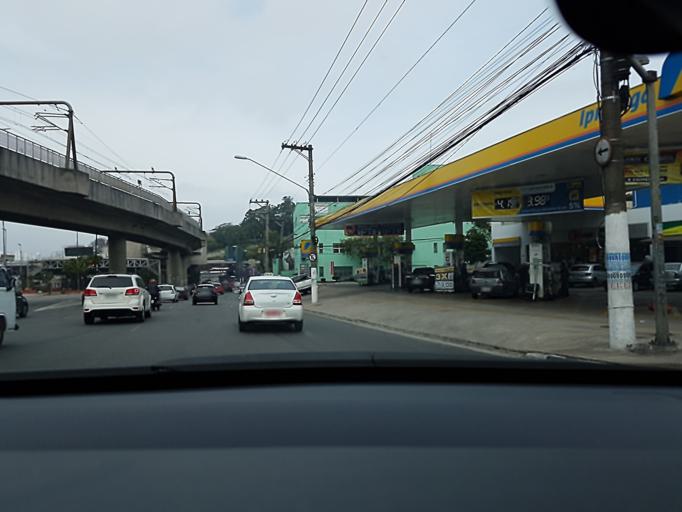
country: BR
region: Sao Paulo
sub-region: Taboao Da Serra
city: Taboao da Serra
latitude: -23.6430
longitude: -46.7364
